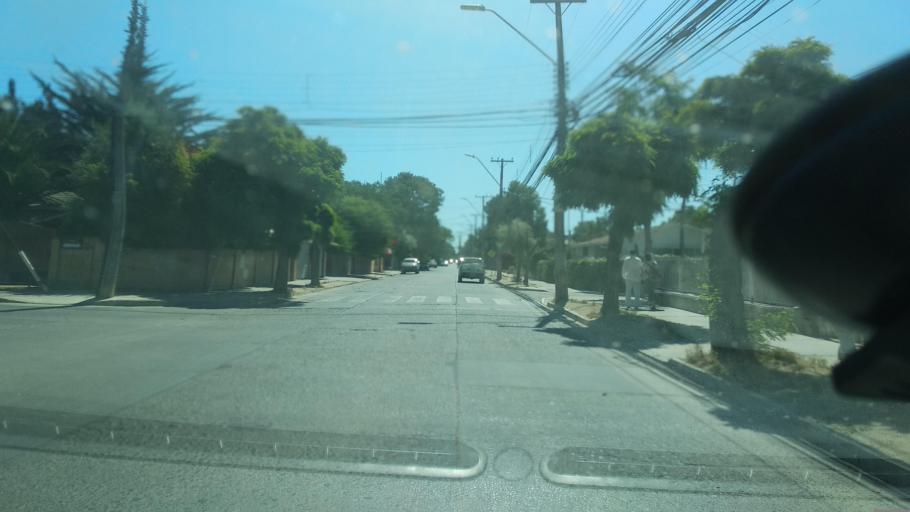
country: CL
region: Valparaiso
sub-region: Provincia de Marga Marga
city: Villa Alemana
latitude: -33.0462
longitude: -71.3665
